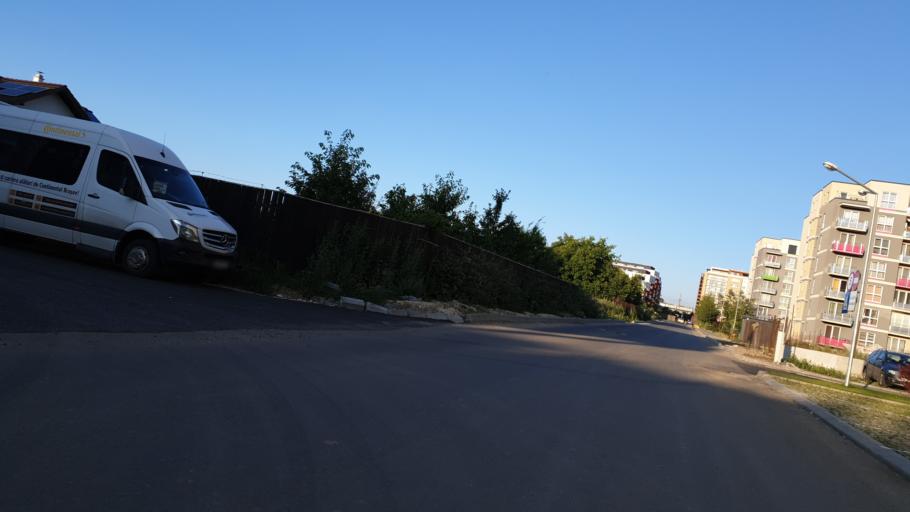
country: RO
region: Brasov
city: Brasov
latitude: 45.6752
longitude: 25.6043
